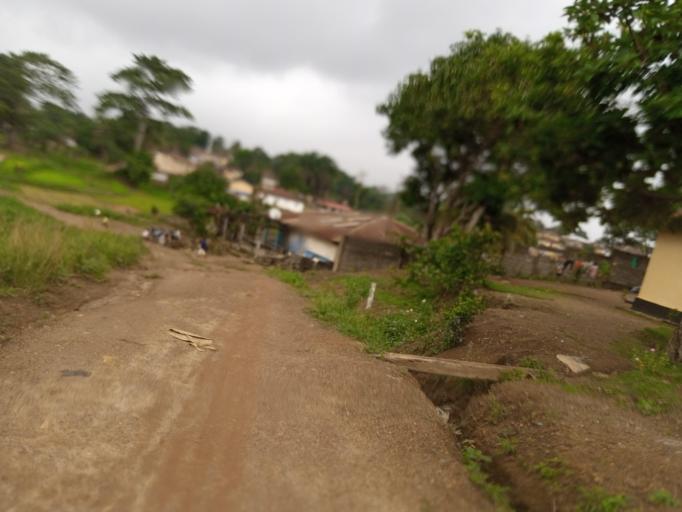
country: SL
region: Eastern Province
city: Kenema
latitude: 7.8789
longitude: -11.1757
